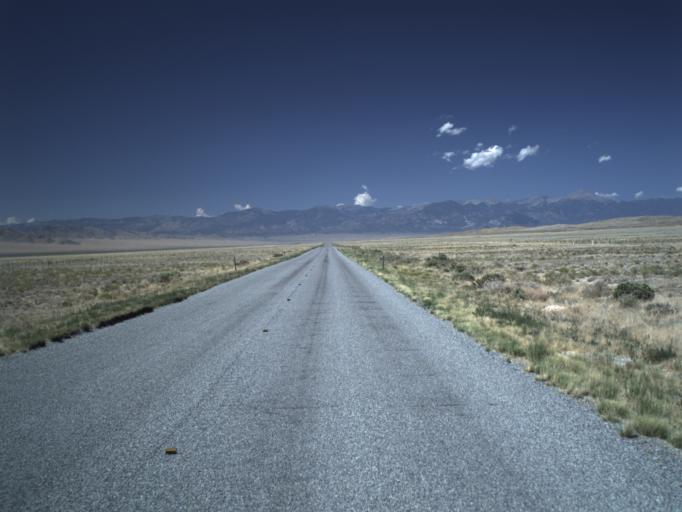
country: US
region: Utah
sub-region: Beaver County
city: Milford
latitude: 39.0525
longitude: -113.7784
